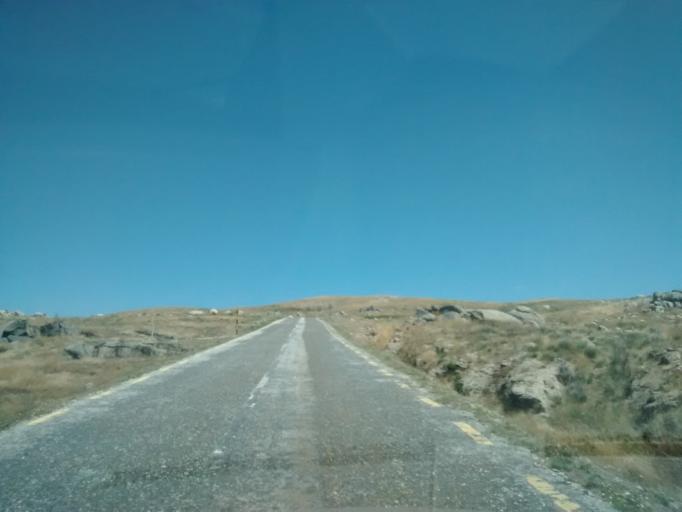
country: PT
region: Guarda
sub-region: Seia
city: Seia
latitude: 40.4125
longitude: -7.6427
